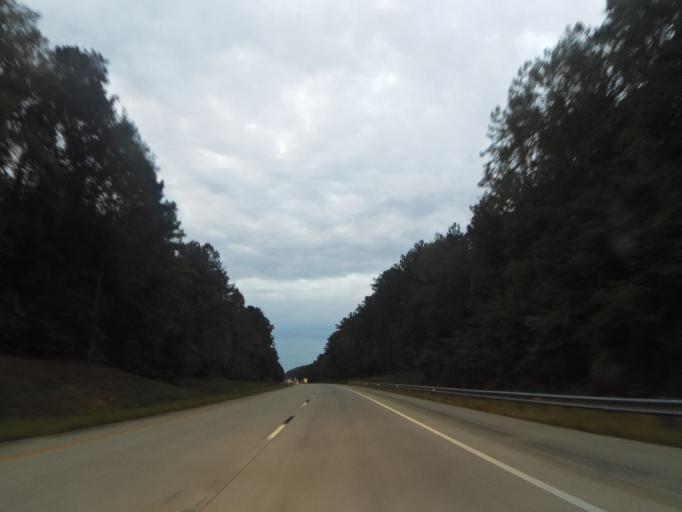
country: US
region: Alabama
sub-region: Etowah County
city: Gadsden
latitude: 34.0547
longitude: -86.0405
